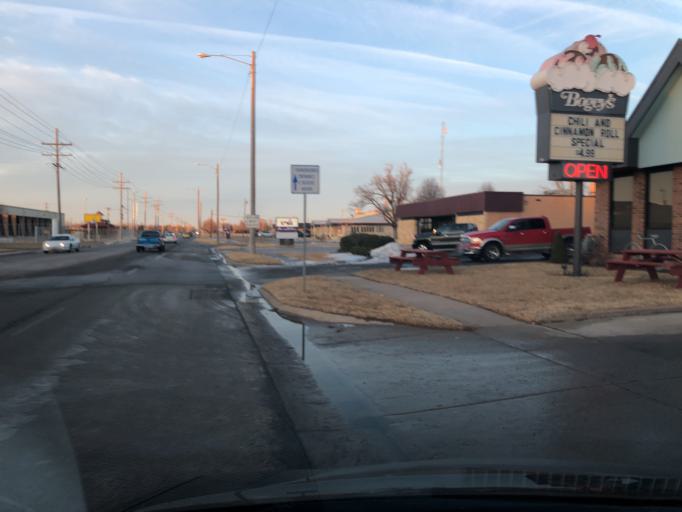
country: US
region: Kansas
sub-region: Reno County
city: Hutchinson
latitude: 38.0731
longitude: -97.9220
